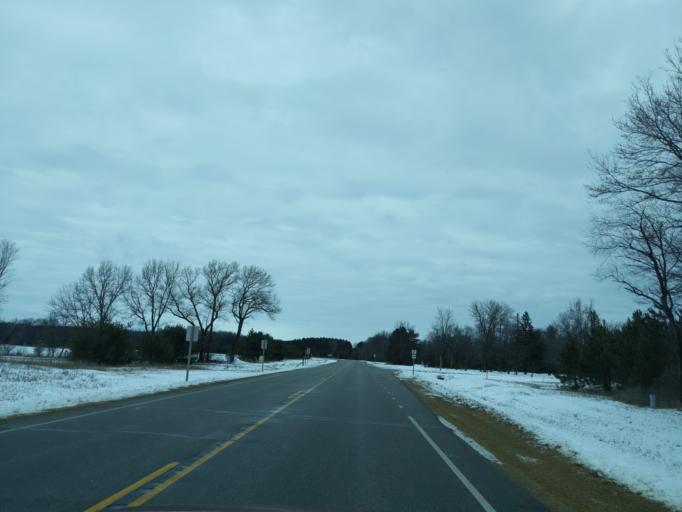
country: US
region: Wisconsin
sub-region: Marquette County
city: Montello
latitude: 43.9333
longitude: -89.3122
